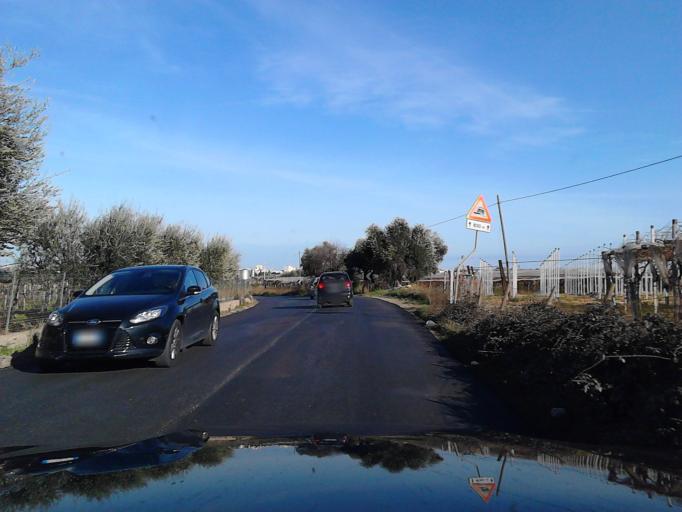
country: IT
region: Apulia
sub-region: Provincia di Bari
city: Noicattaro
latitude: 41.0172
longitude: 16.9656
